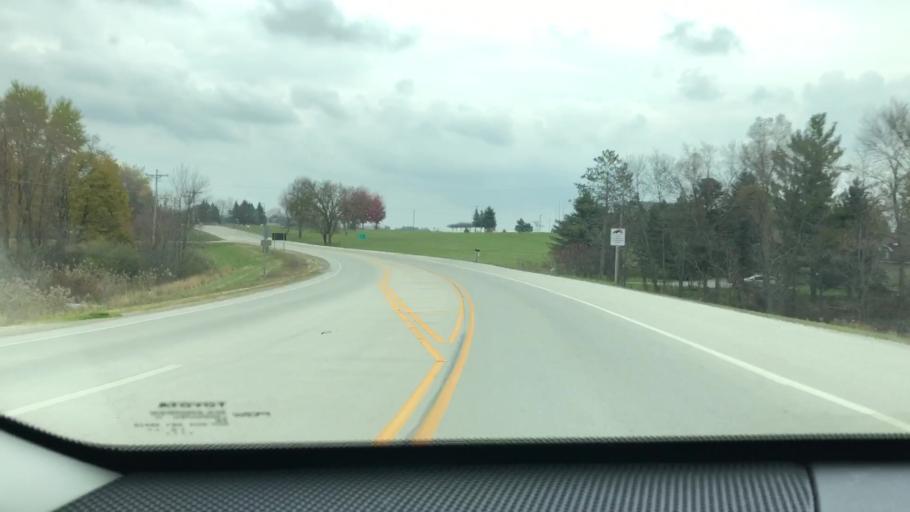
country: US
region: Wisconsin
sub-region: Brown County
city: Oneida
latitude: 44.4987
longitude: -88.1740
